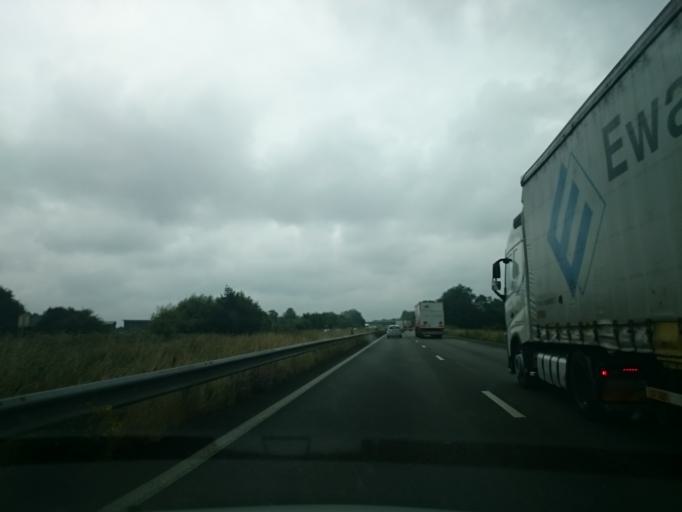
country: FR
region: Pays de la Loire
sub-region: Departement de la Loire-Atlantique
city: Sautron
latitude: 47.2733
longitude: -1.7182
